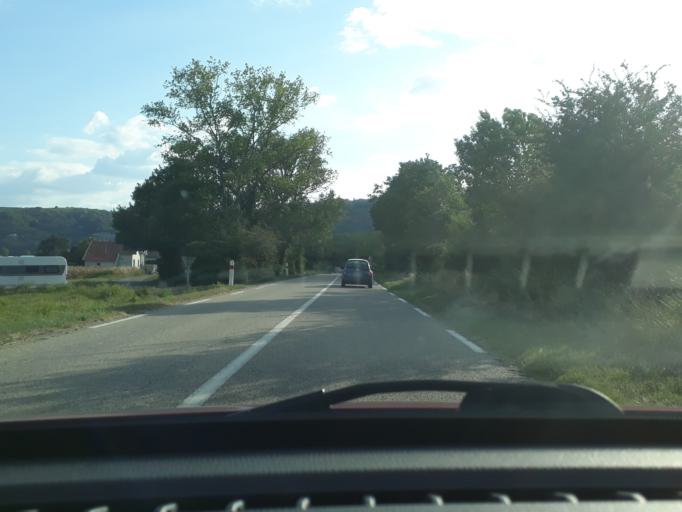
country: FR
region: Rhone-Alpes
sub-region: Departement de l'Isere
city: Sablons
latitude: 45.3315
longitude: 4.7708
